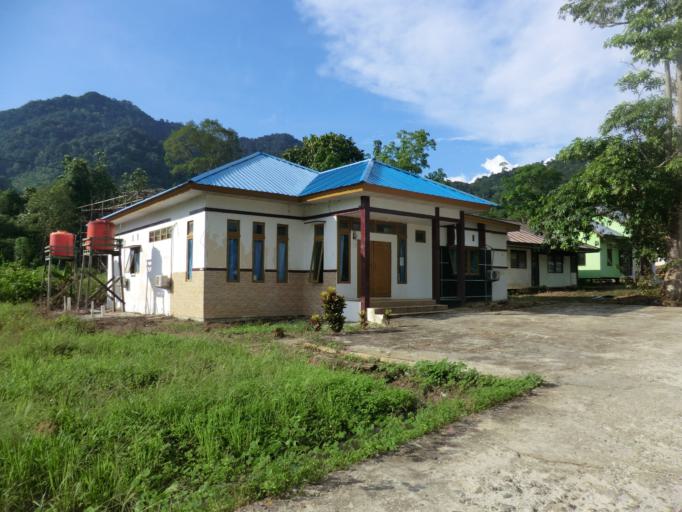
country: MY
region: Sarawak
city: Simanggang
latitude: 1.0367
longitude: 112.2286
